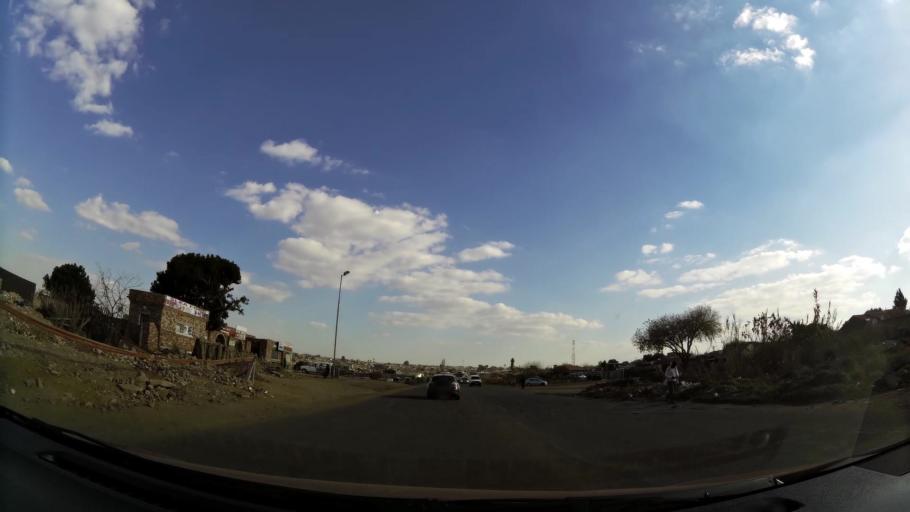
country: ZA
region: Gauteng
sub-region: Ekurhuleni Metropolitan Municipality
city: Tembisa
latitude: -26.0006
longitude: 28.1833
